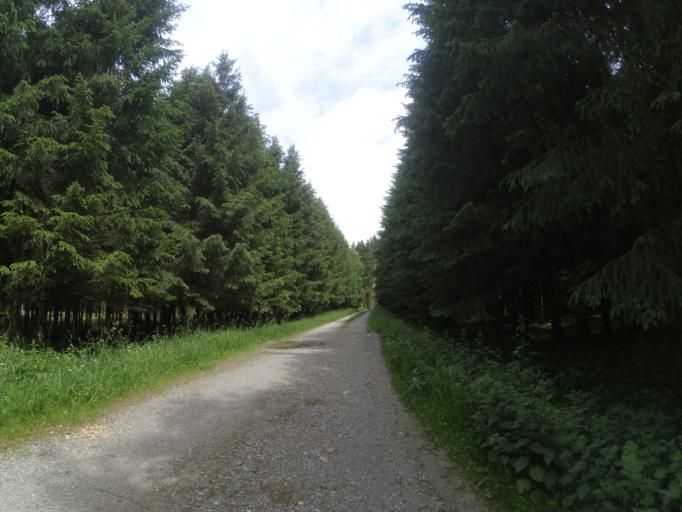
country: DE
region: Baden-Wuerttemberg
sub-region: Tuebingen Region
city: Leutkirch im Allgau
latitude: 47.7719
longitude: 10.0058
